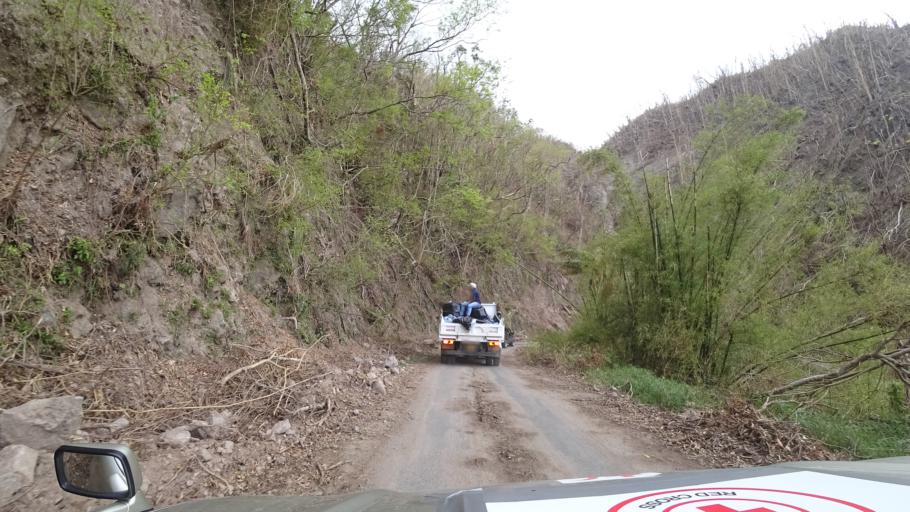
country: DM
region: Saint Mark
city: Soufriere
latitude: 15.2398
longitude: -61.3643
